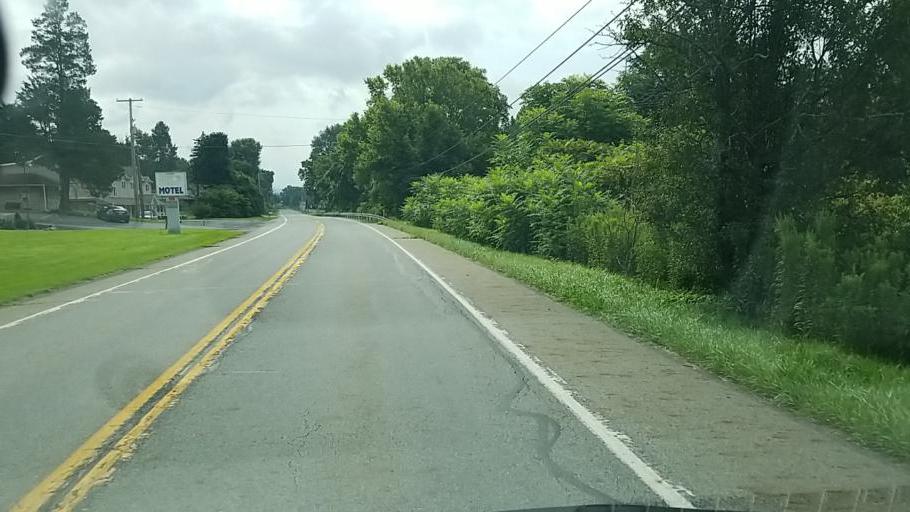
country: US
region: Pennsylvania
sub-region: Dauphin County
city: Millersburg
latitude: 40.5095
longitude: -76.9635
